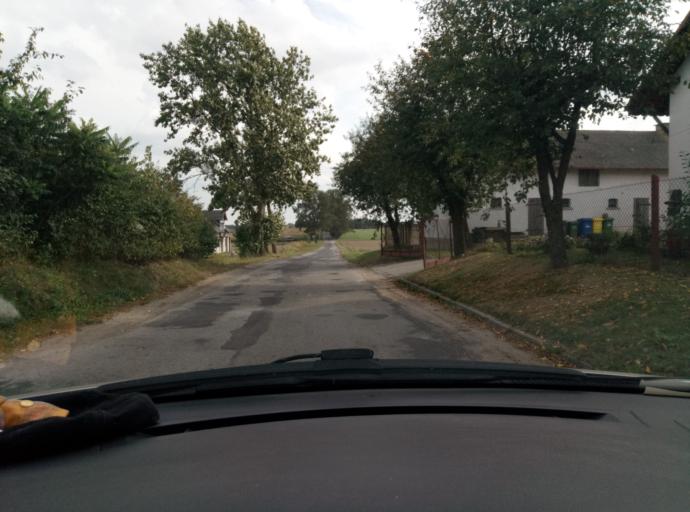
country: PL
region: Kujawsko-Pomorskie
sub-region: Powiat brodnicki
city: Jablonowo Pomorskie
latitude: 53.3850
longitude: 19.2456
